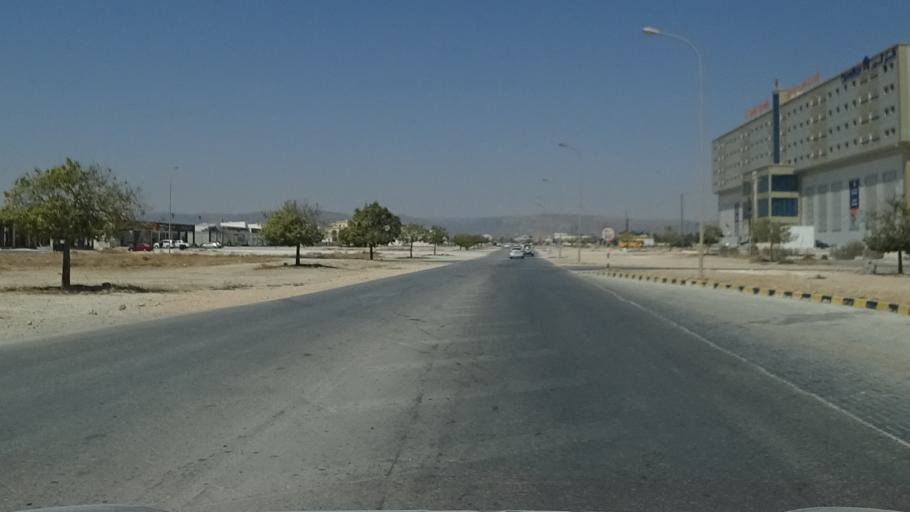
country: OM
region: Zufar
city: Salalah
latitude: 17.0502
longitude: 54.1676
